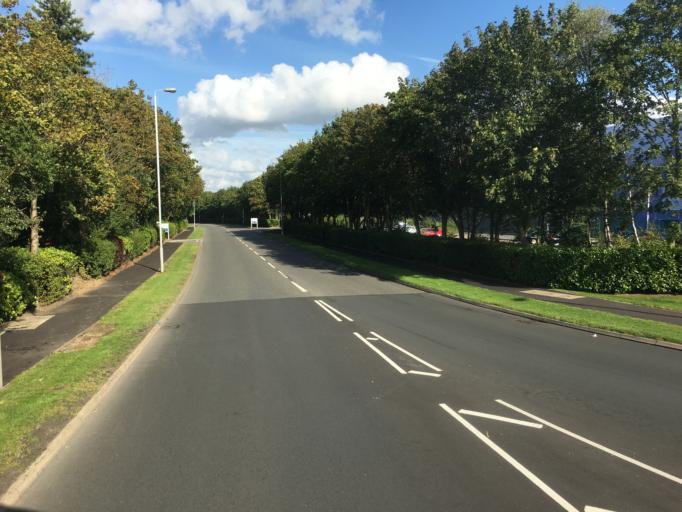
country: GB
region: England
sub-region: Leicestershire
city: Lutterworth
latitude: 52.4547
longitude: -1.2493
